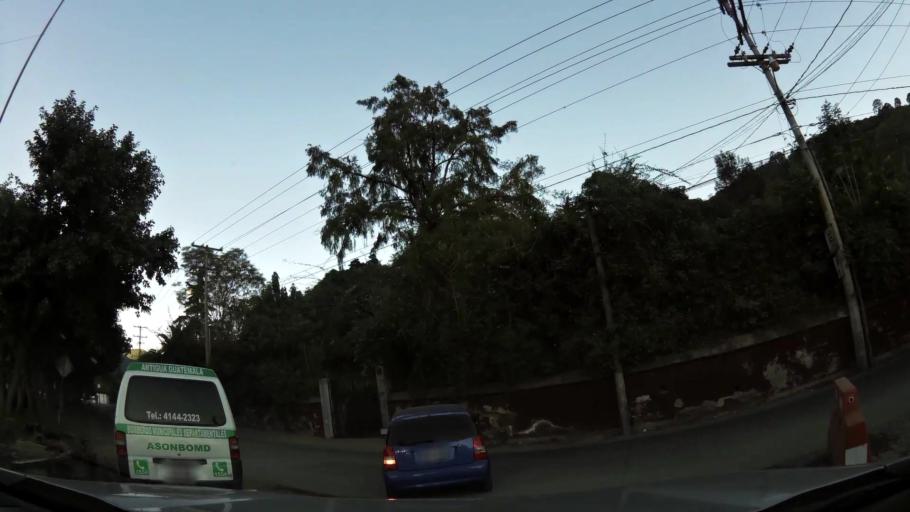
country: GT
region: Sacatepequez
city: Antigua Guatemala
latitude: 14.5575
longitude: -90.7264
